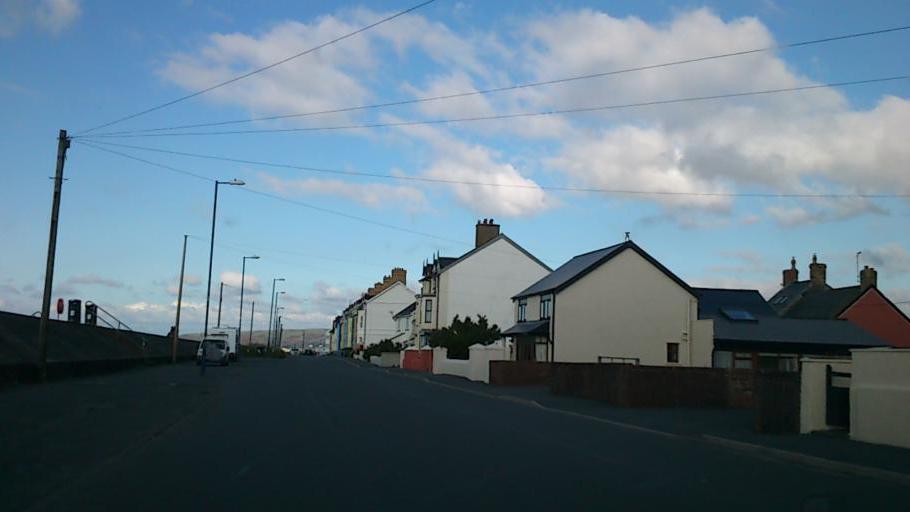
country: GB
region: Wales
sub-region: County of Ceredigion
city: Bow Street
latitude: 52.4941
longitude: -4.0517
